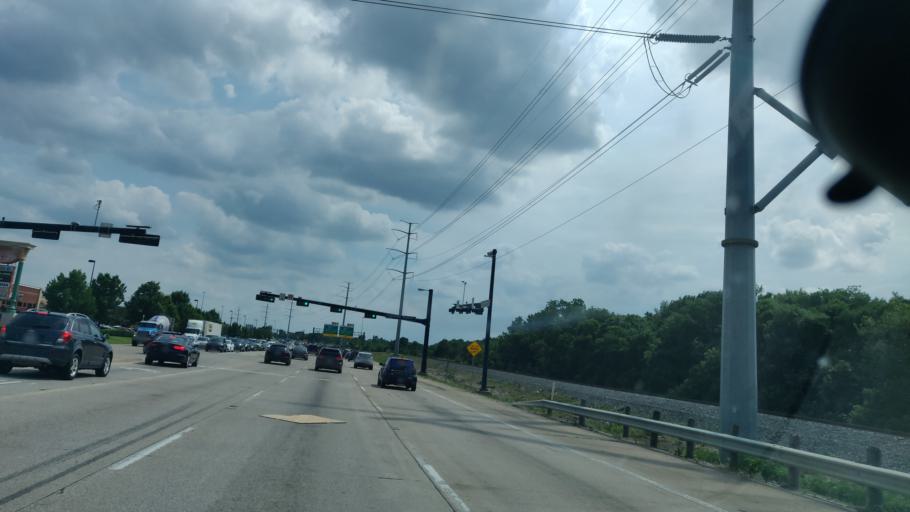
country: US
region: Texas
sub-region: Dallas County
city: Sachse
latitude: 32.9589
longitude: -96.6155
